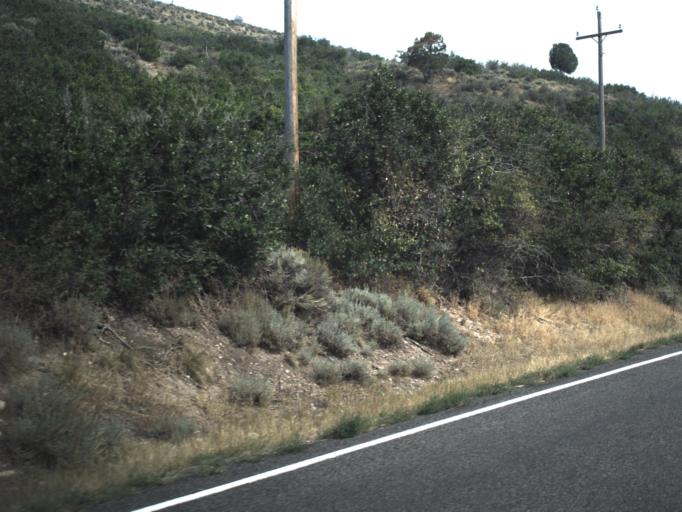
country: US
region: Utah
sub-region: Summit County
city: Kamas
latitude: 40.6358
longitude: -111.2567
